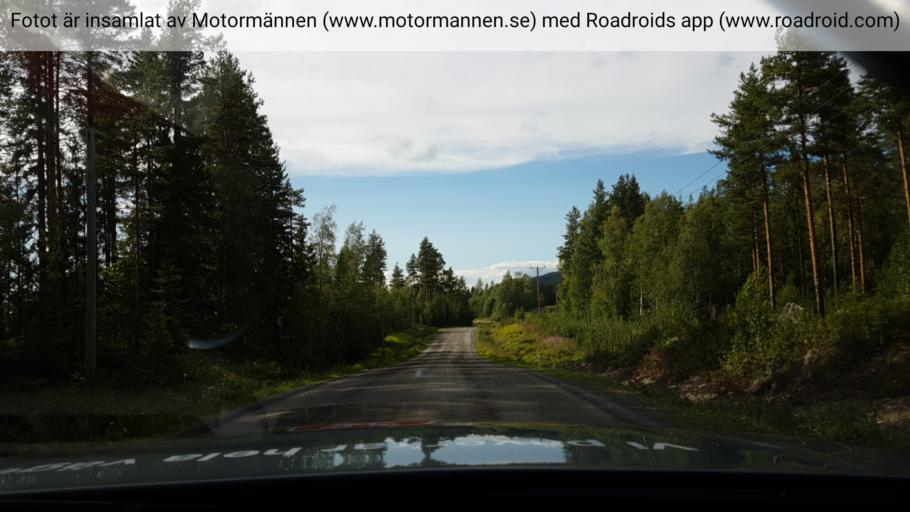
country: SE
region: Jaemtland
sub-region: Braecke Kommun
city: Braecke
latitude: 63.1917
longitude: 15.5191
